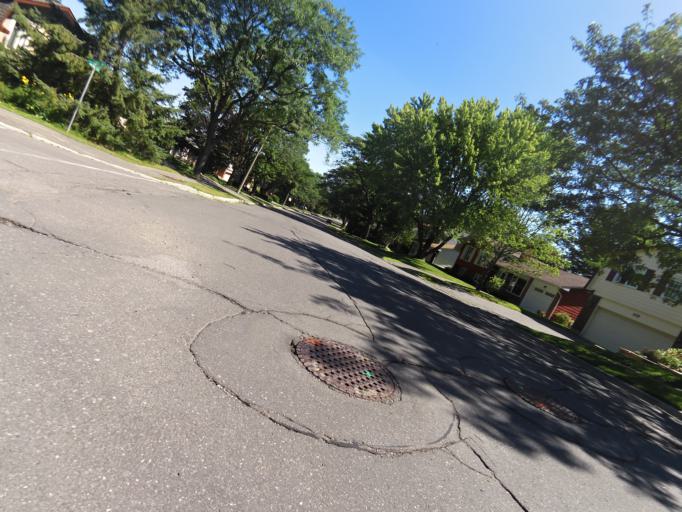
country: CA
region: Ontario
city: Ottawa
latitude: 45.3523
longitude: -75.6632
